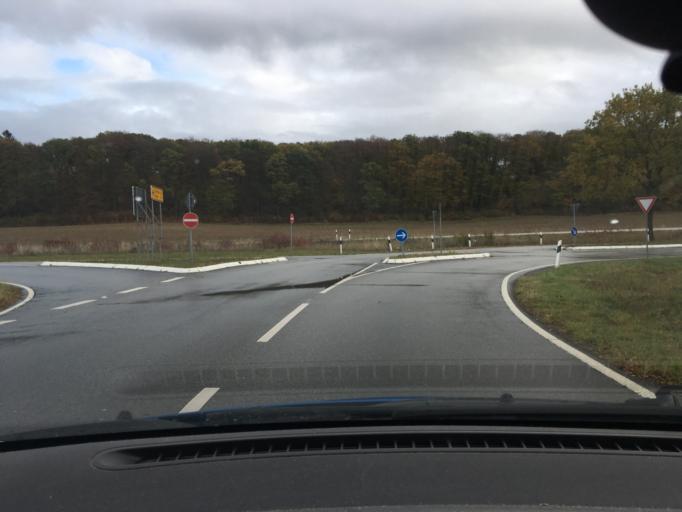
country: DE
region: Schleswig-Holstein
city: Fredeburg
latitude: 53.6457
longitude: 10.7010
